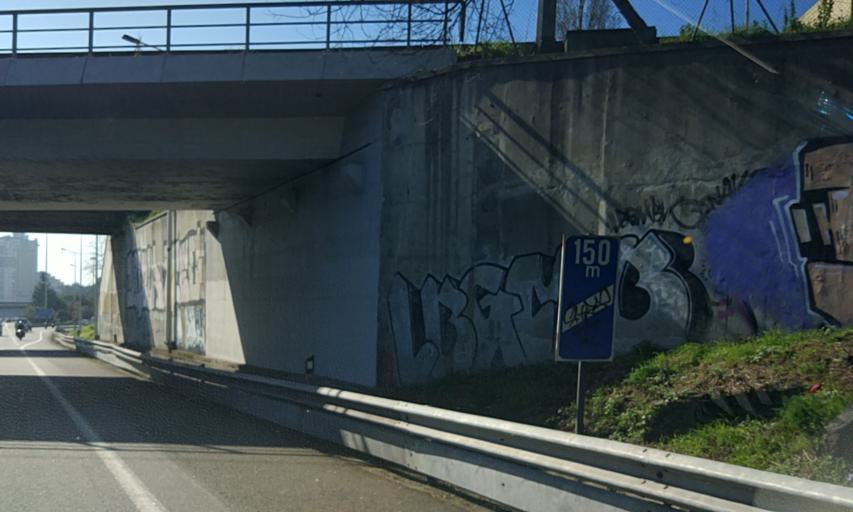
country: PT
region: Porto
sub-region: Matosinhos
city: Senhora da Hora
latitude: 41.1700
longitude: -8.6351
